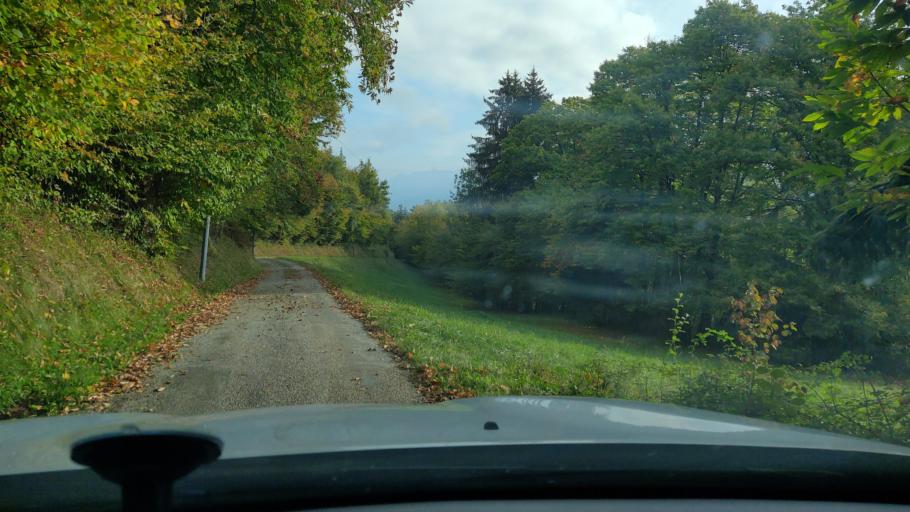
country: FR
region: Rhone-Alpes
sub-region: Departement de la Savoie
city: La Rochette
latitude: 45.4768
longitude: 6.1113
